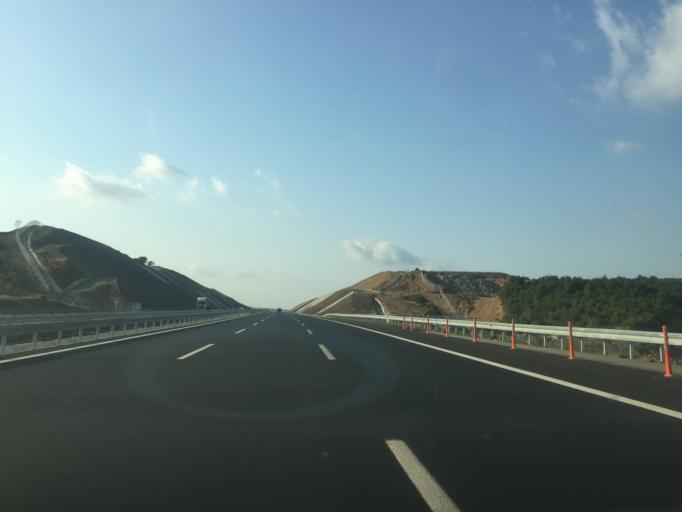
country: TR
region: Balikesir
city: Ertugrul
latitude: 39.5230
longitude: 27.6806
